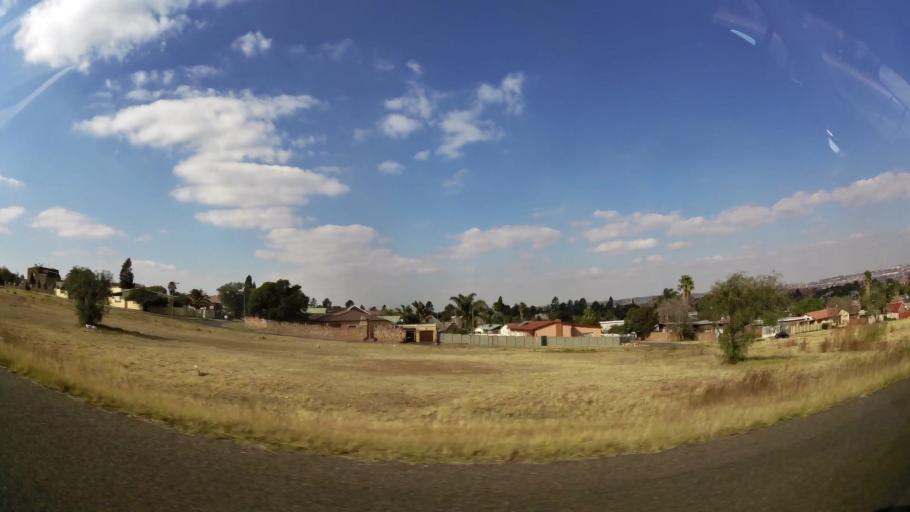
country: ZA
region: Gauteng
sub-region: West Rand District Municipality
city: Krugersdorp
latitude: -26.0768
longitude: 27.7607
